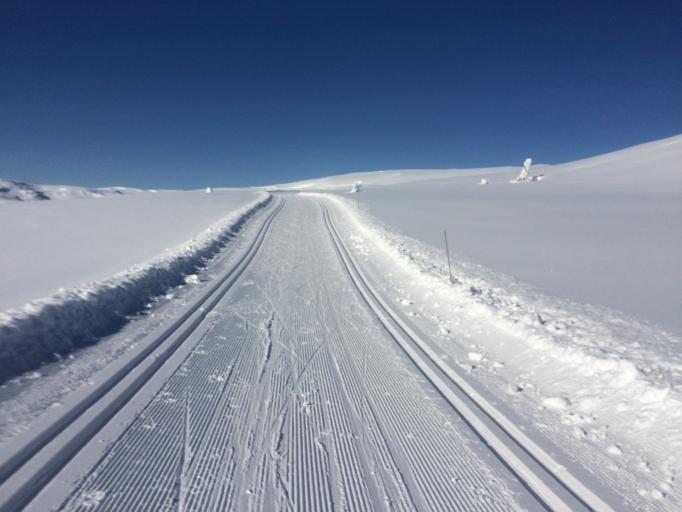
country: NO
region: Oppland
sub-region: Ringebu
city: Ringebu
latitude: 61.3675
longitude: 10.0749
